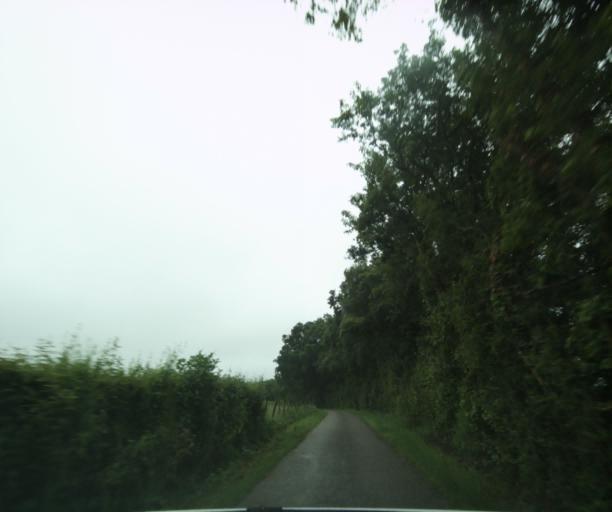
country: FR
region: Bourgogne
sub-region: Departement de Saone-et-Loire
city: Charolles
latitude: 46.3936
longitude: 4.1969
